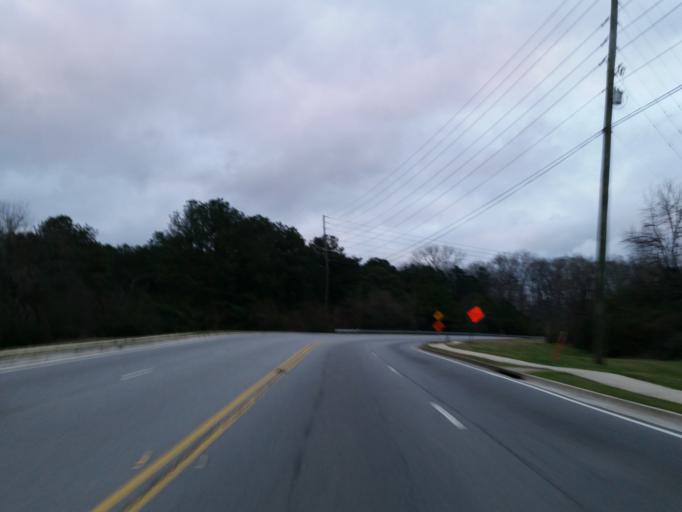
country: US
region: Georgia
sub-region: Cobb County
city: Fair Oaks
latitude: 33.9016
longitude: -84.5789
